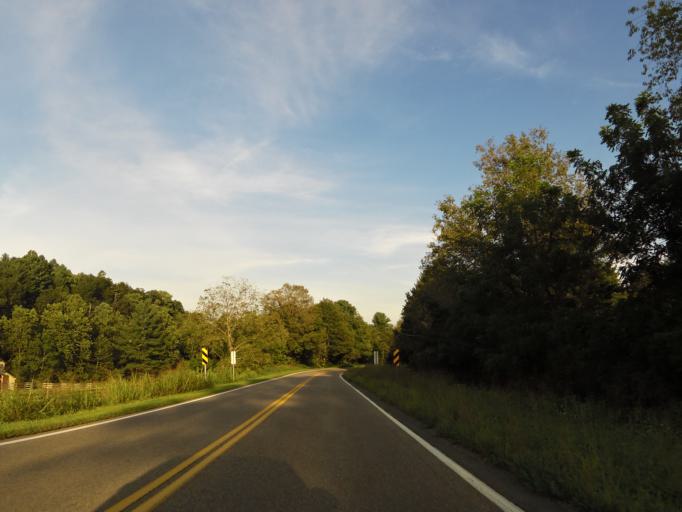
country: US
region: Virginia
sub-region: Washington County
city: Emory
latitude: 36.6490
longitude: -81.8323
